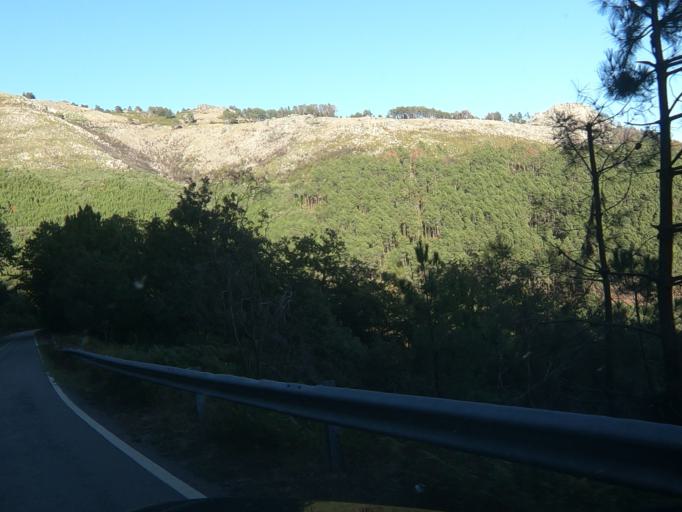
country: PT
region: Vila Real
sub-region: Vila Real
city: Vila Real
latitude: 41.3378
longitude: -7.7818
